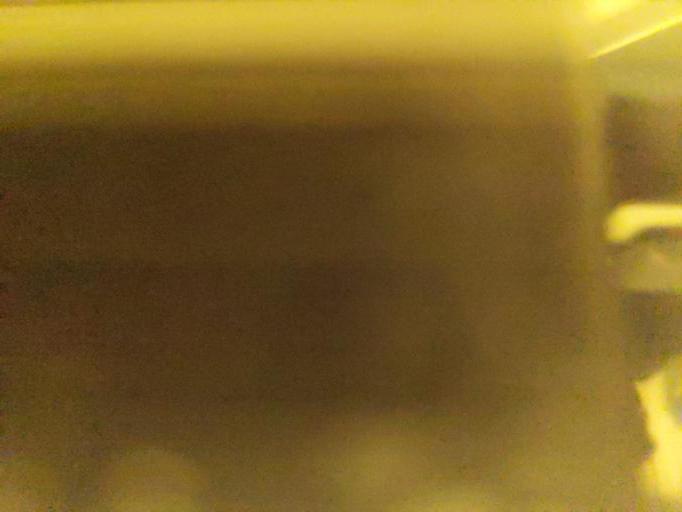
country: JP
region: Kanagawa
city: Odawara
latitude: 35.2184
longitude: 139.1380
